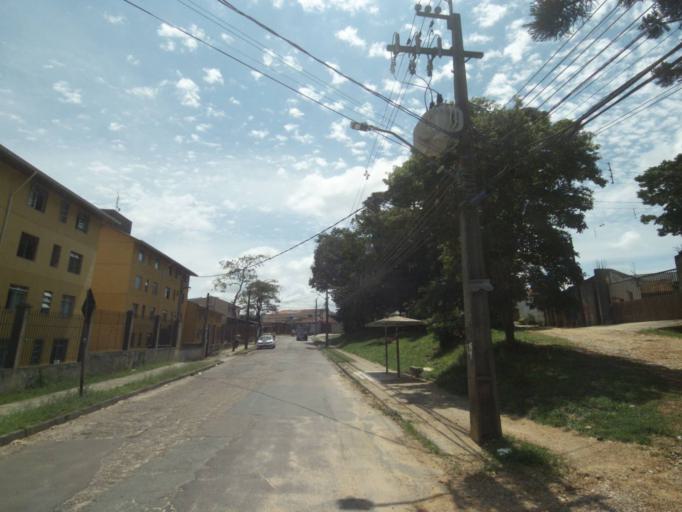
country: BR
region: Parana
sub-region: Curitiba
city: Curitiba
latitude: -25.4584
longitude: -49.3494
